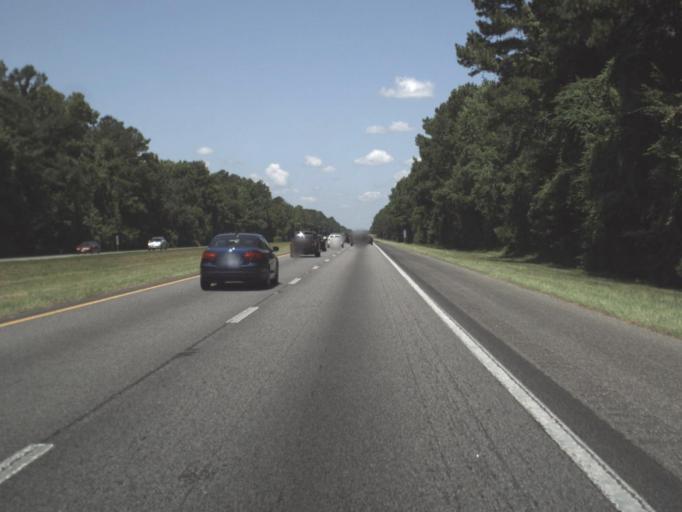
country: US
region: Florida
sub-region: Jefferson County
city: Monticello
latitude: 30.4450
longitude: -83.6943
